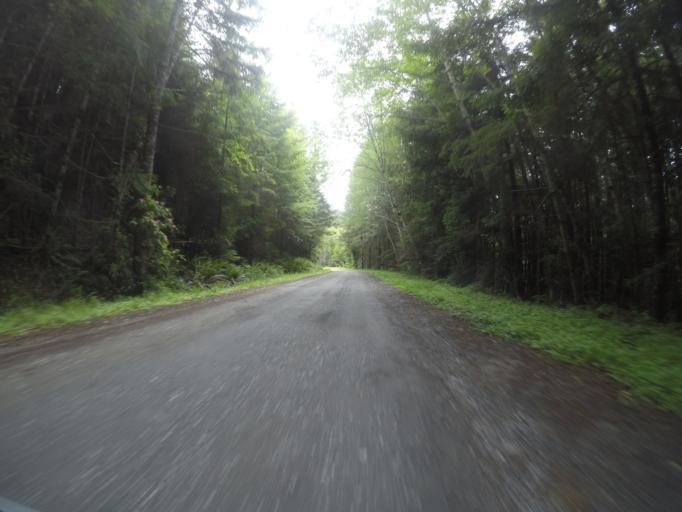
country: US
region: California
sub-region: Humboldt County
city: Westhaven-Moonstone
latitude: 41.2330
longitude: -123.9901
